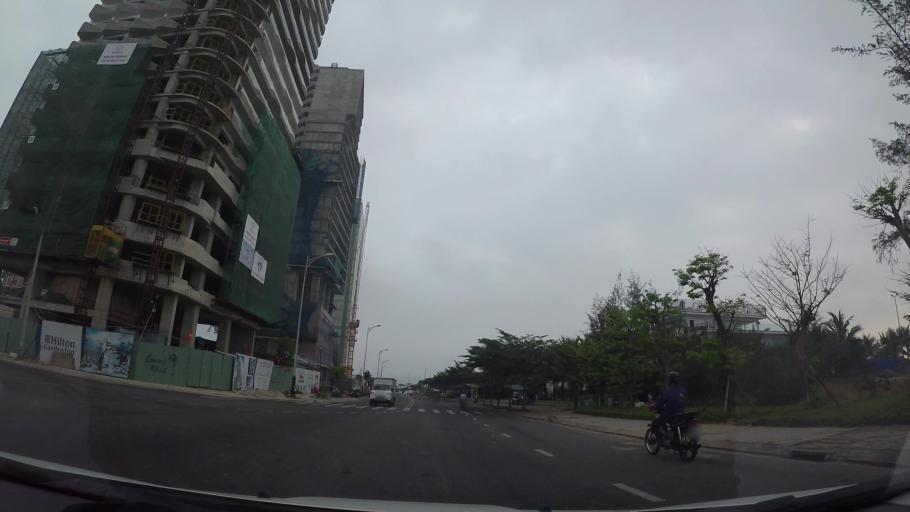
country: VN
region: Da Nang
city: Son Tra
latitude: 16.0797
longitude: 108.2465
